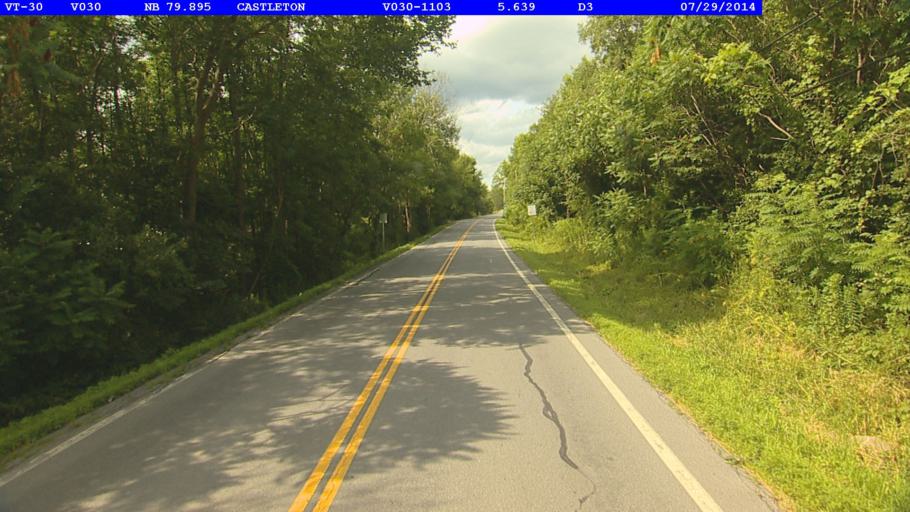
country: US
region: Vermont
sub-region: Rutland County
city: Castleton
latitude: 43.6659
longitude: -73.1915
